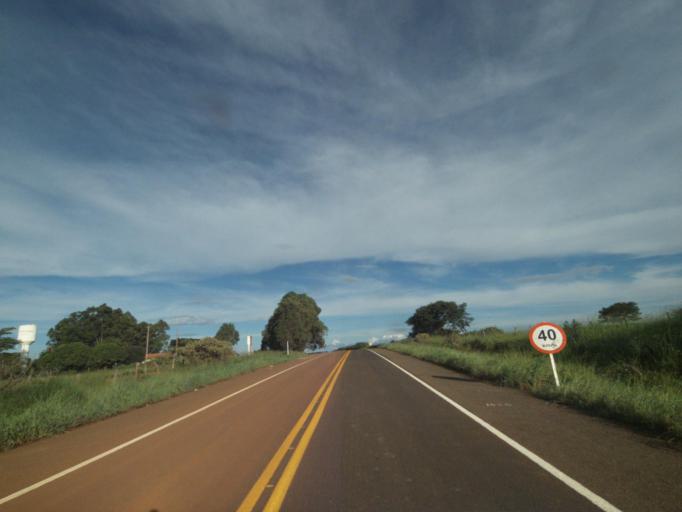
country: BR
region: Goias
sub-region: Jaragua
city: Jaragua
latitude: -15.8950
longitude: -49.5021
